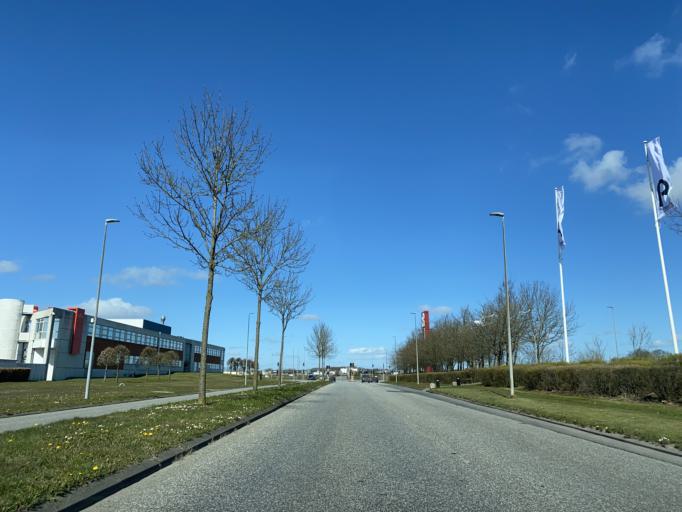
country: DK
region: Central Jutland
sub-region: Randers Kommune
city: Randers
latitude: 56.4290
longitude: 10.0615
